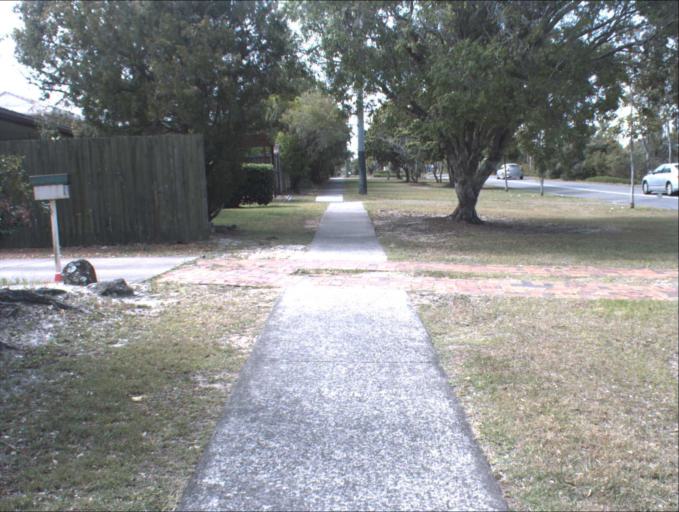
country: AU
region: Queensland
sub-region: Logan
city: Springwood
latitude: -27.6201
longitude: 153.1429
